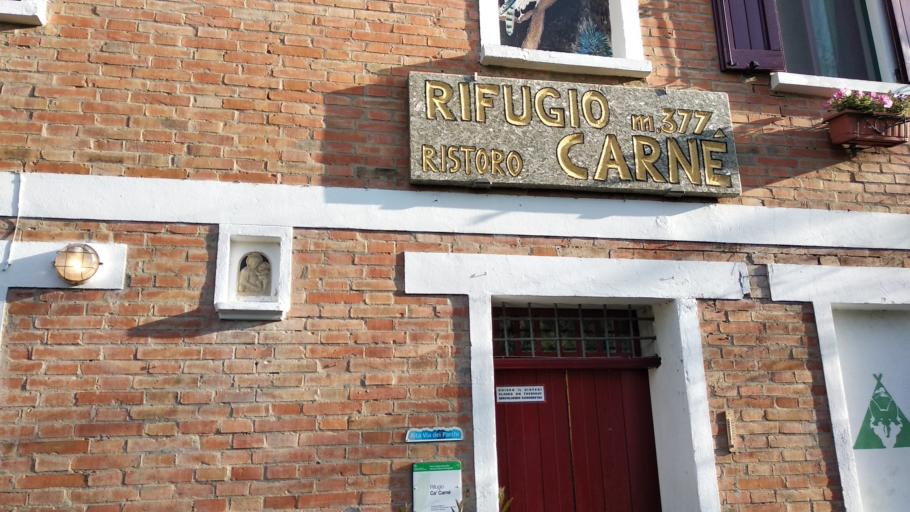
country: IT
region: Emilia-Romagna
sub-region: Provincia di Ravenna
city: Fognano
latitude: 44.2269
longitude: 11.7377
